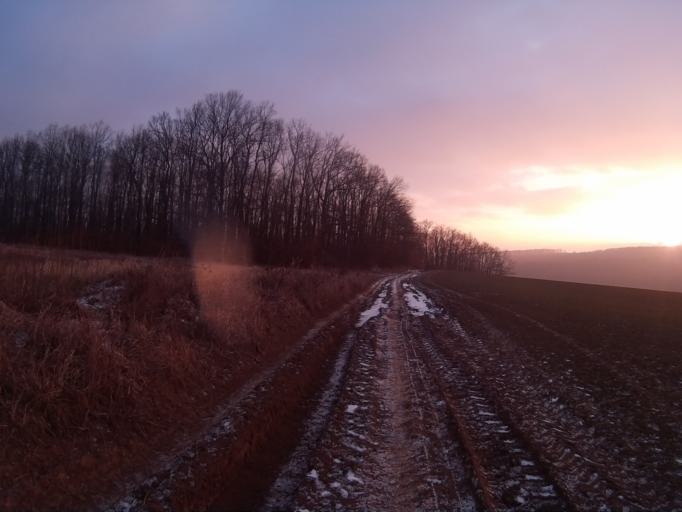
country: HU
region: Borsod-Abauj-Zemplen
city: Szendro
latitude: 48.4144
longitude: 20.8734
